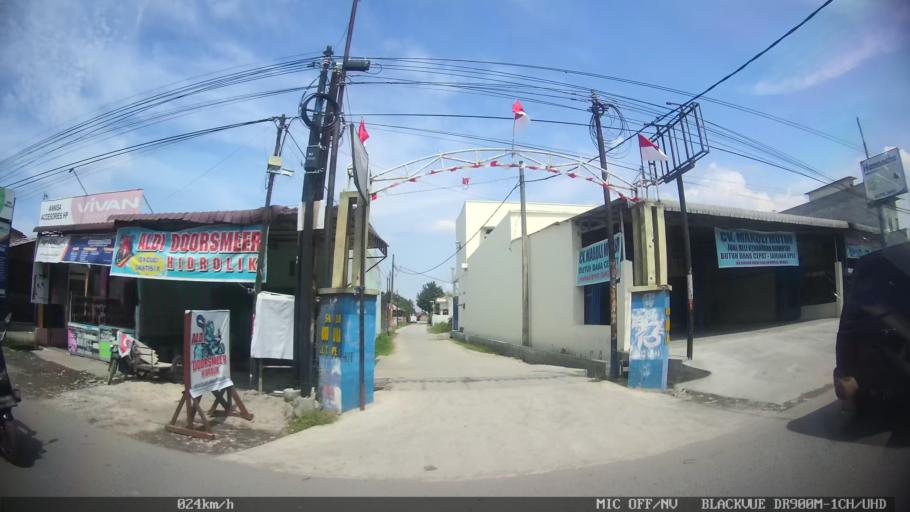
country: ID
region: North Sumatra
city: Labuhan Deli
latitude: 3.6723
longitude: 98.6560
